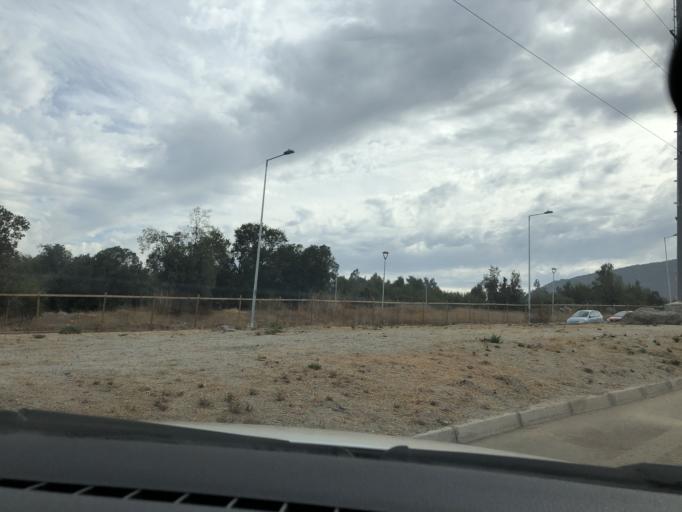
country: CL
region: Santiago Metropolitan
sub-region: Provincia de Cordillera
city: Puente Alto
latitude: -33.5816
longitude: -70.5164
